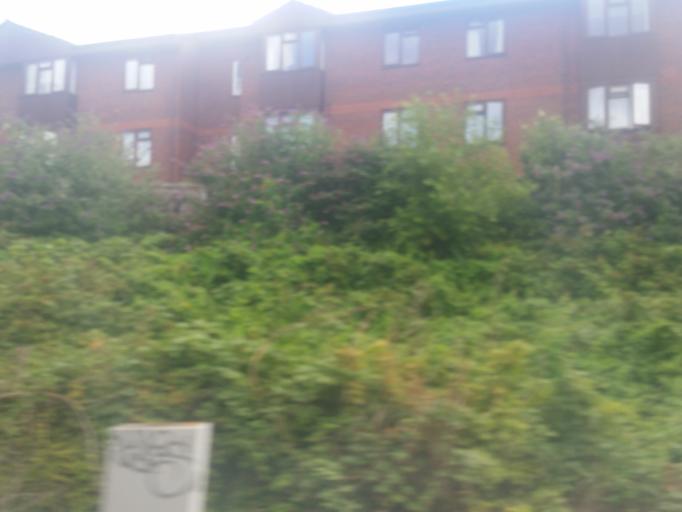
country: GB
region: England
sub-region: Greater London
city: Thornton Heath
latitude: 51.4008
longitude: -0.0725
